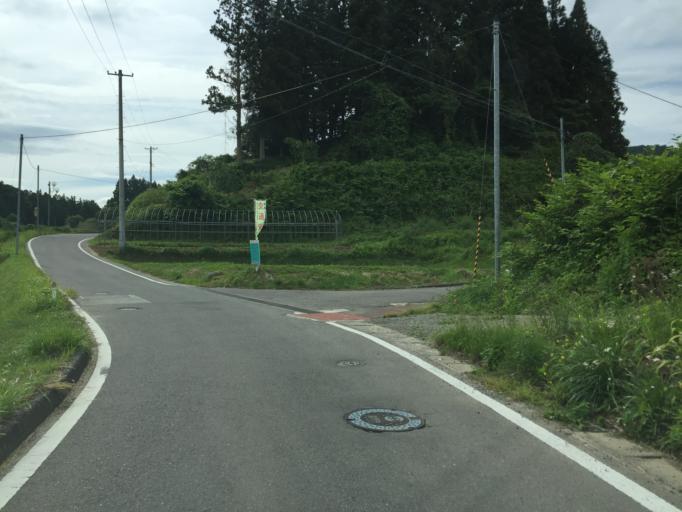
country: JP
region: Fukushima
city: Funehikimachi-funehiki
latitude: 37.4589
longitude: 140.6410
